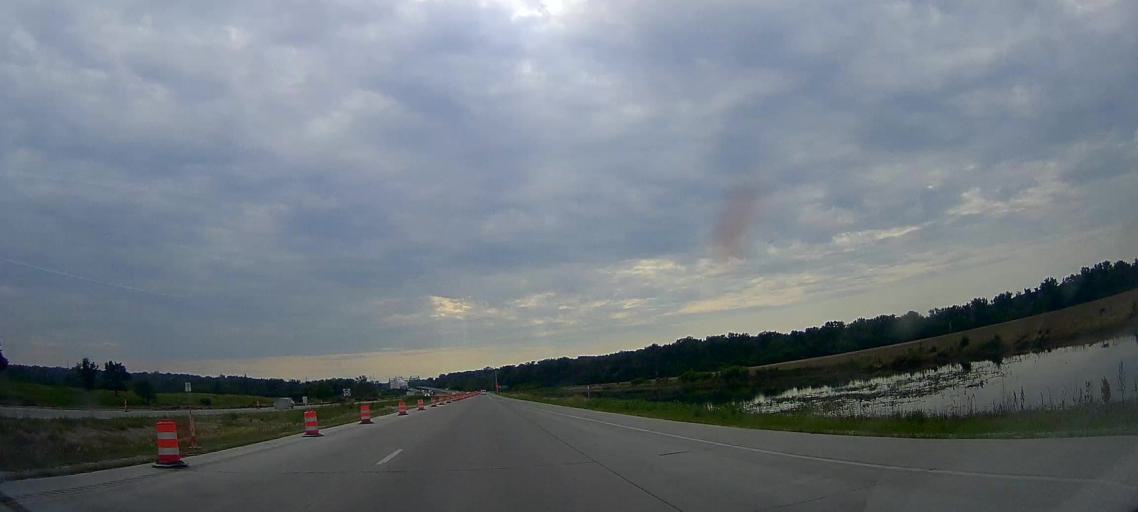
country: US
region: Iowa
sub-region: Pottawattamie County
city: Carter Lake
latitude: 41.3467
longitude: -95.9434
